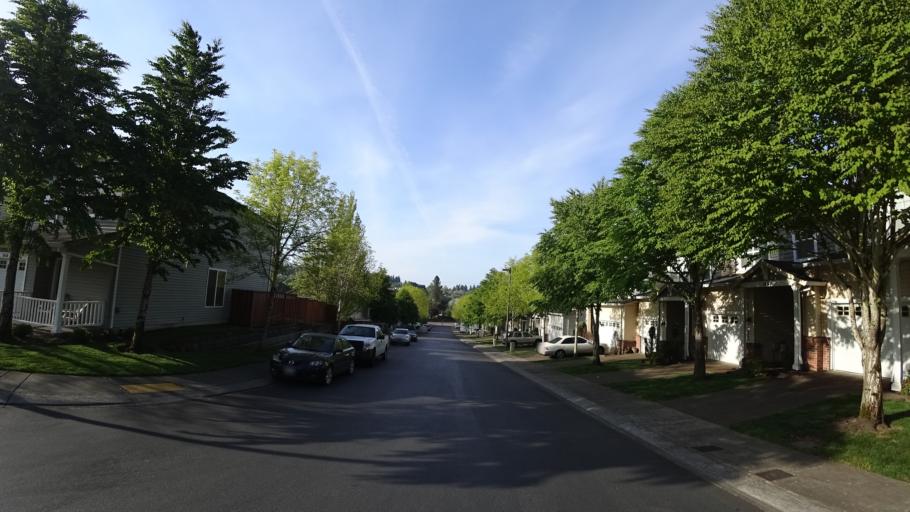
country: US
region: Oregon
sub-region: Washington County
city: King City
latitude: 45.4283
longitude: -122.8441
